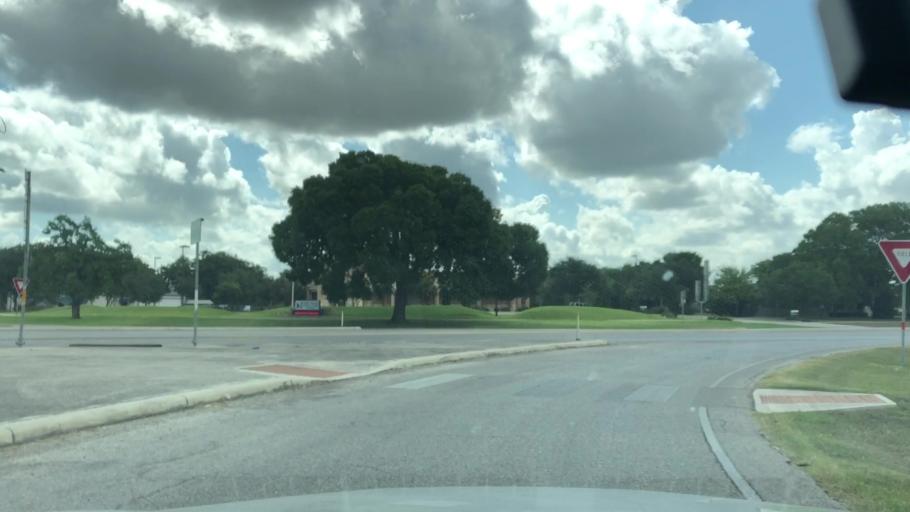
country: US
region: Texas
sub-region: Guadalupe County
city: Seguin
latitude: 29.5691
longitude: -97.9891
